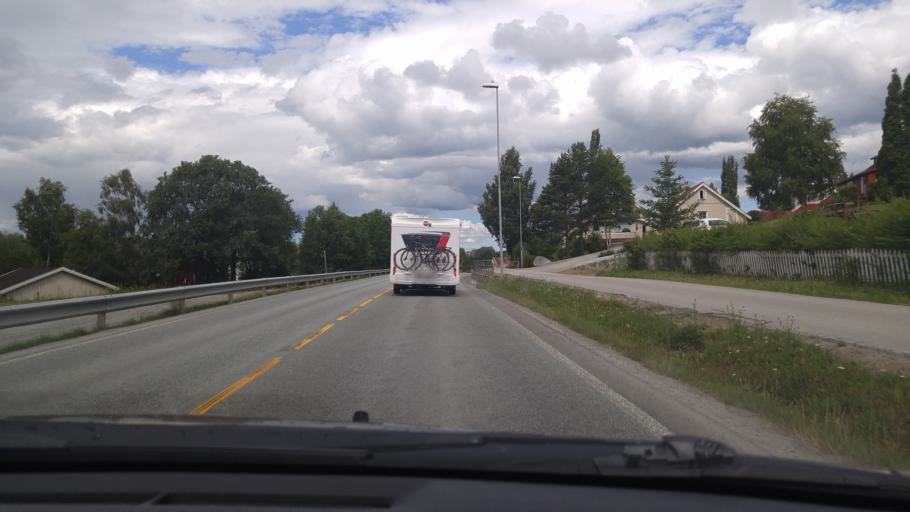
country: NO
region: Nord-Trondelag
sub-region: Steinkjer
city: Steinkjer
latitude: 63.9198
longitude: 11.4326
